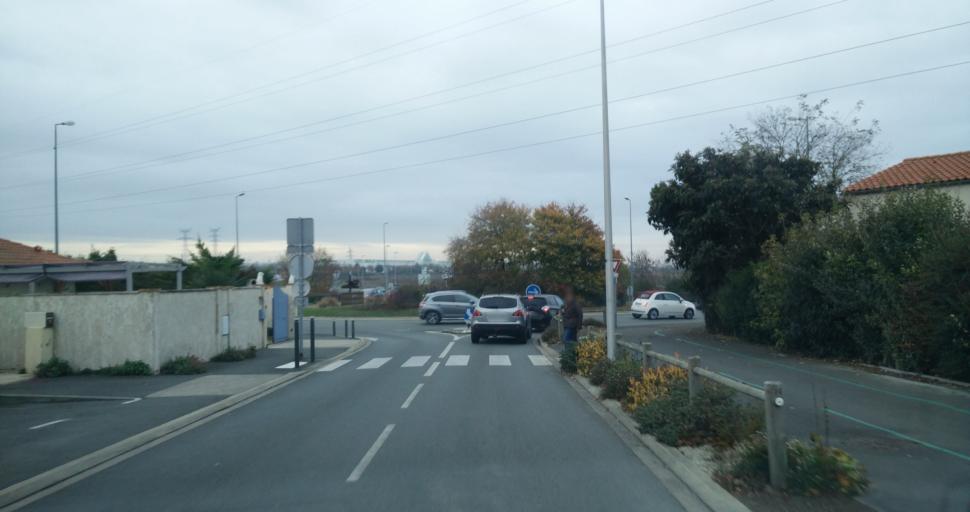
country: FR
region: Poitou-Charentes
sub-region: Departement de la Charente-Maritime
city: Puilboreau
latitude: 46.1818
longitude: -1.1251
